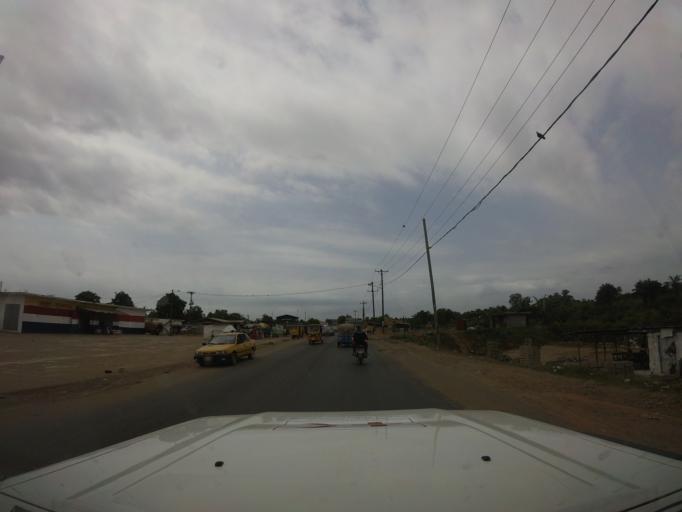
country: LR
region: Montserrado
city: Monrovia
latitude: 6.3839
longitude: -10.7818
